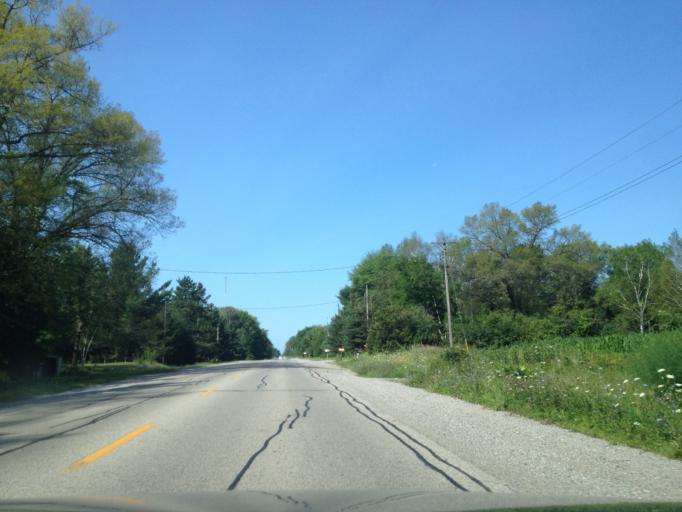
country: CA
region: Ontario
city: Norfolk County
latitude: 42.8108
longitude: -80.3805
